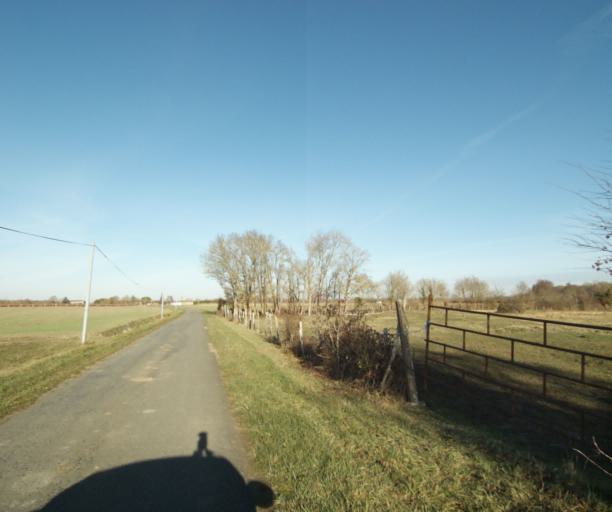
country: FR
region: Poitou-Charentes
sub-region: Departement de la Charente-Maritime
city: Burie
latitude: 45.7905
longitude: -0.4178
